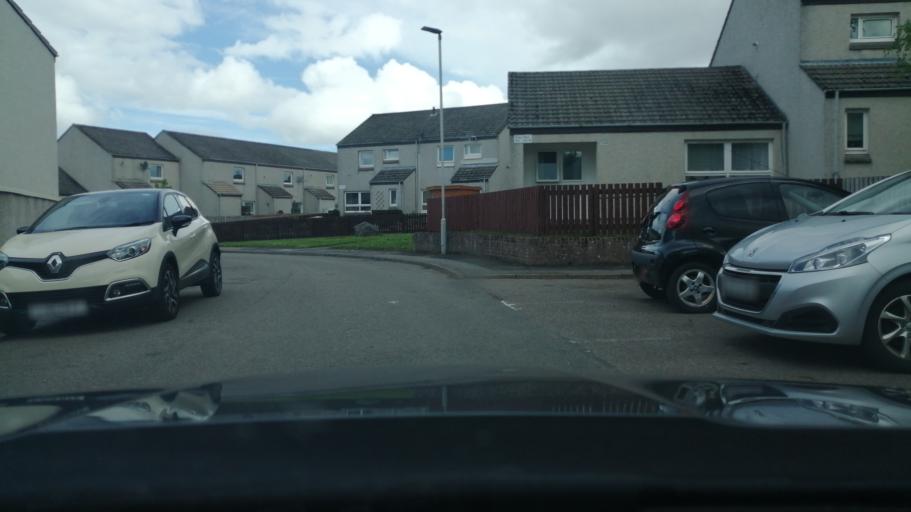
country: GB
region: Scotland
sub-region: Moray
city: Keith
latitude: 57.5344
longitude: -2.9425
